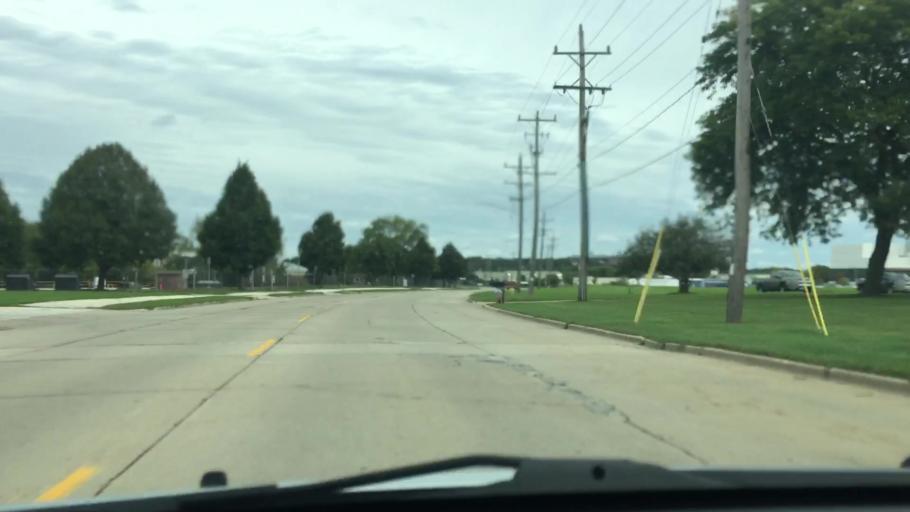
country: US
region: Wisconsin
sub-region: Waukesha County
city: Waukesha
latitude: 42.9936
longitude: -88.2497
